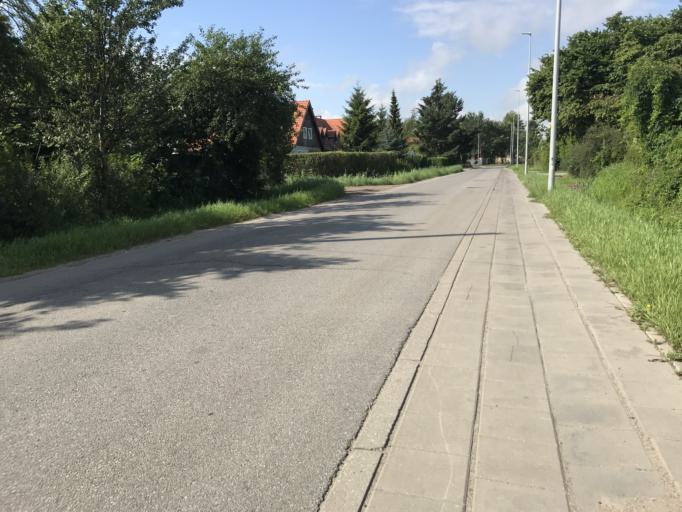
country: PL
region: Pomeranian Voivodeship
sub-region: Gdansk
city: Gdansk
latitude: 54.3347
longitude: 18.6605
